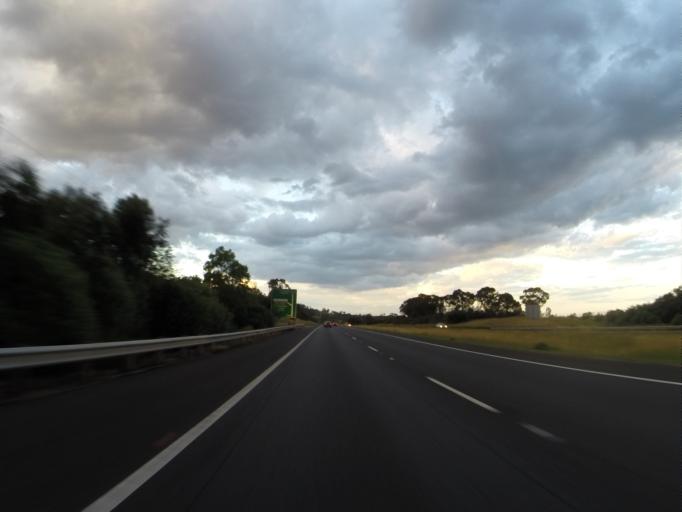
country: AU
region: New South Wales
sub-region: Campbelltown Municipality
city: Glen Alpine
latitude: -34.0721
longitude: 150.7771
